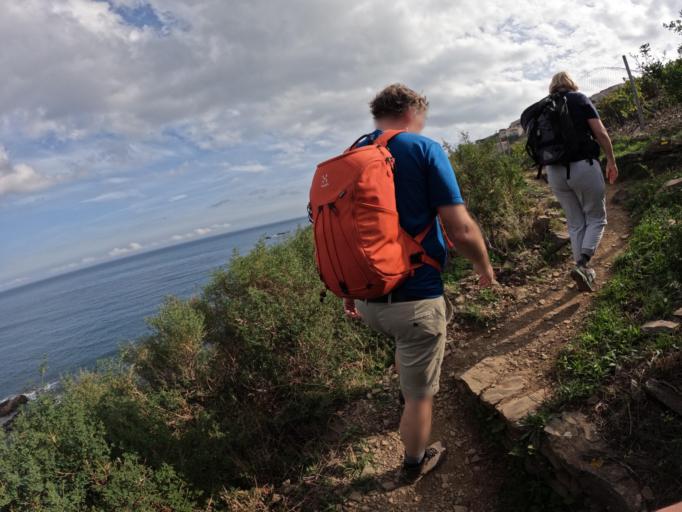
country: FR
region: Languedoc-Roussillon
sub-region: Departement des Pyrenees-Orientales
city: Cervera de la Marenda
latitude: 42.4501
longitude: 3.1630
